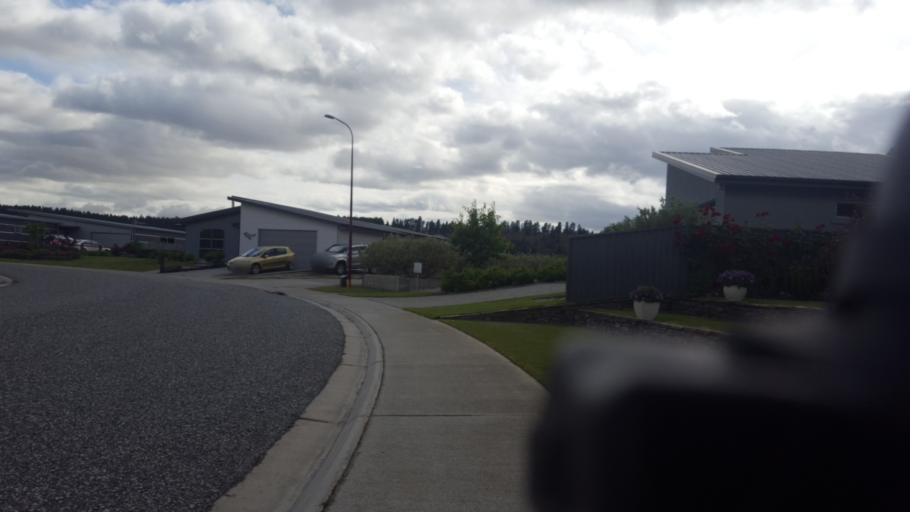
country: NZ
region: Otago
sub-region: Queenstown-Lakes District
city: Wanaka
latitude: -45.2403
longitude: 169.3820
